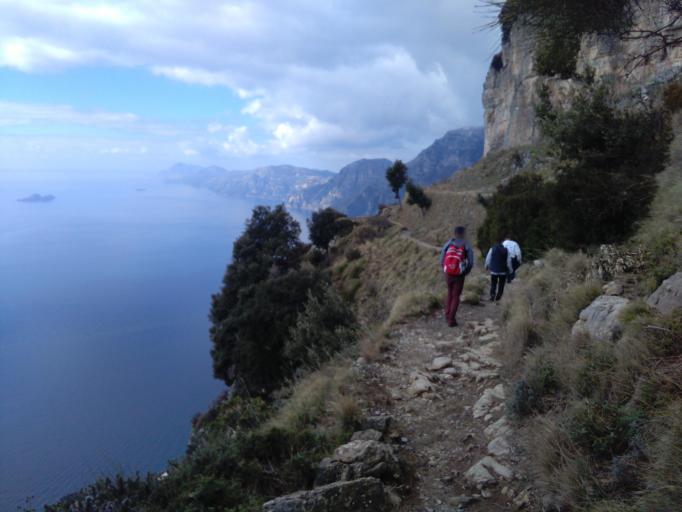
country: IT
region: Campania
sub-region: Provincia di Salerno
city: Praiano
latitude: 40.6217
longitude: 14.5208
